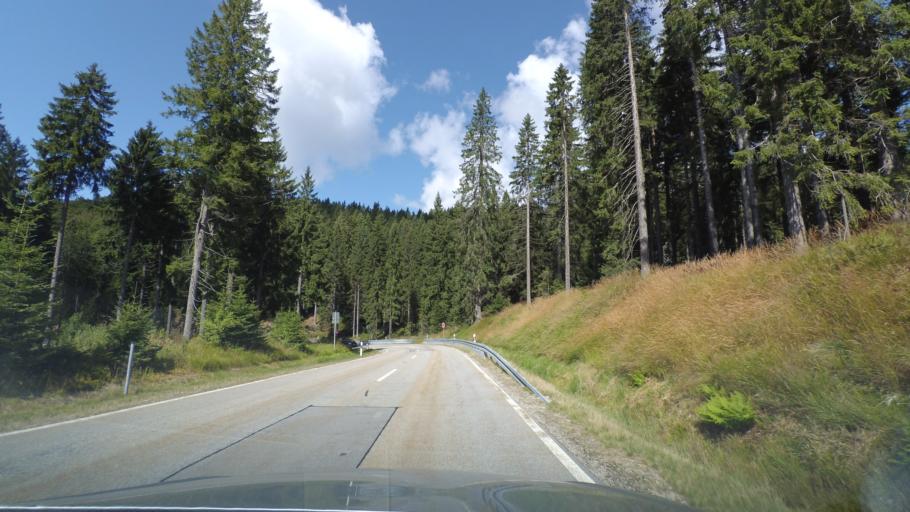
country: DE
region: Bavaria
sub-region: Lower Bavaria
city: Bodenmais
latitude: 49.0743
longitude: 13.1529
